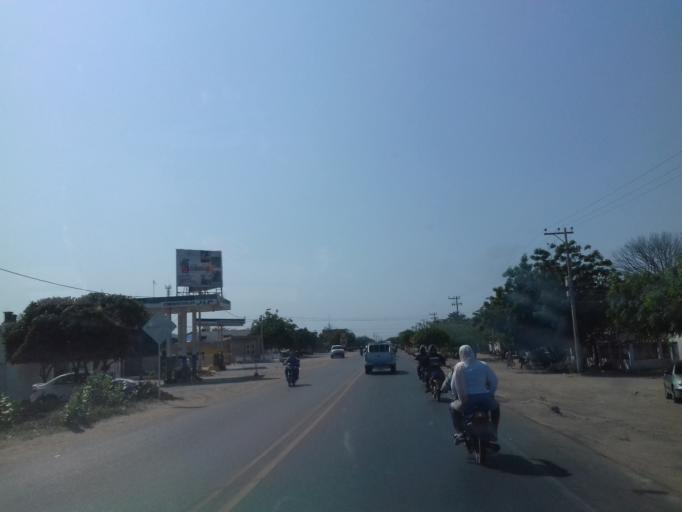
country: CO
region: La Guajira
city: Maicao
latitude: 11.3791
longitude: -72.2498
